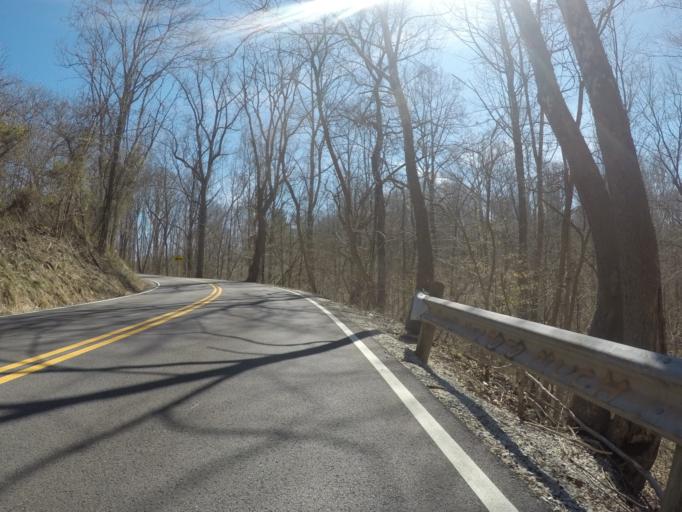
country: US
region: Ohio
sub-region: Lawrence County
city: South Point
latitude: 38.4589
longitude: -82.5538
